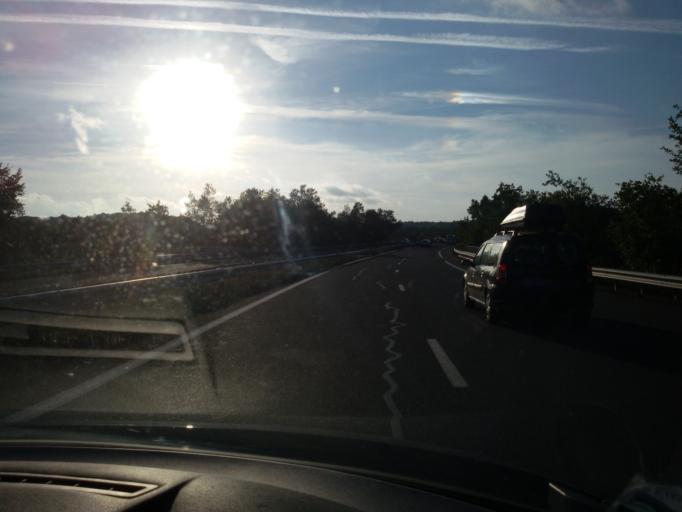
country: FR
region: Languedoc-Roussillon
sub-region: Departement de l'Herault
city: Lodeve
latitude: 43.8890
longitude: 3.2887
